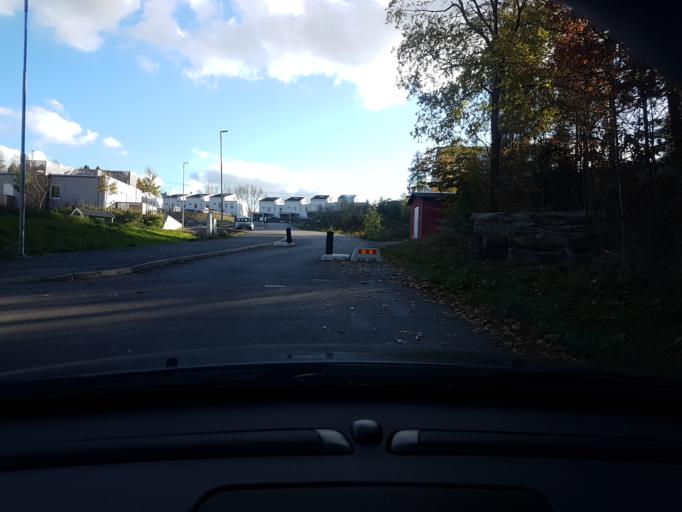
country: SE
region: Vaestra Goetaland
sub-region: Ale Kommun
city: Surte
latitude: 57.8182
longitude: 12.0254
